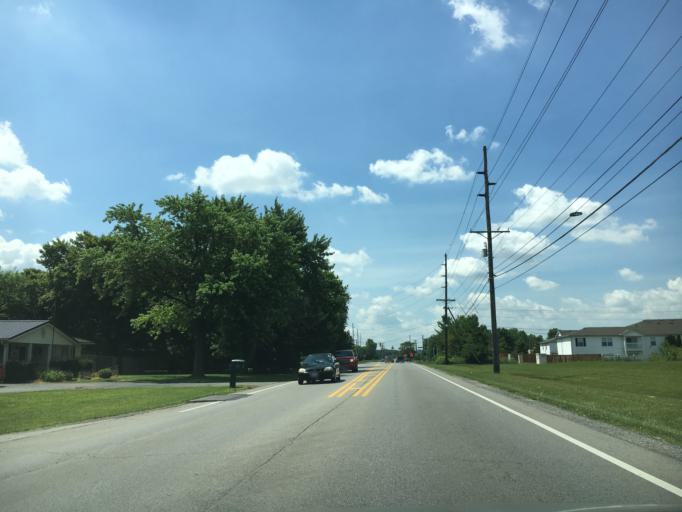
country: US
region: Ohio
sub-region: Franklin County
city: Lincoln Village
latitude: 39.9174
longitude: -83.1440
